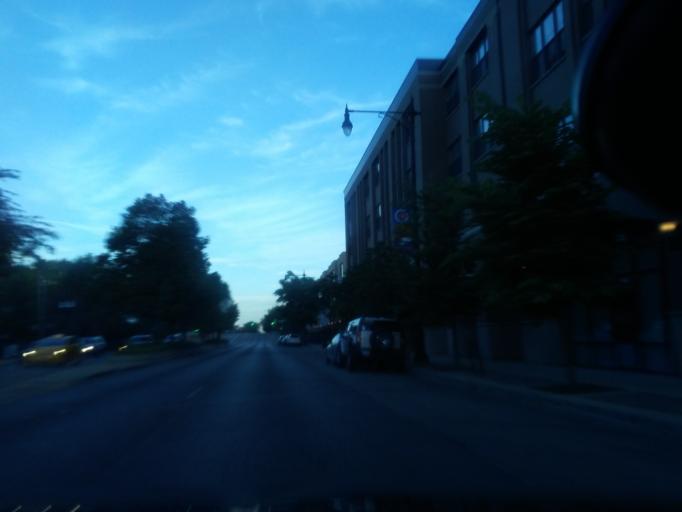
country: US
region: Illinois
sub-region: Cook County
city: Lincolnwood
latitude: 41.9541
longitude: -87.6912
